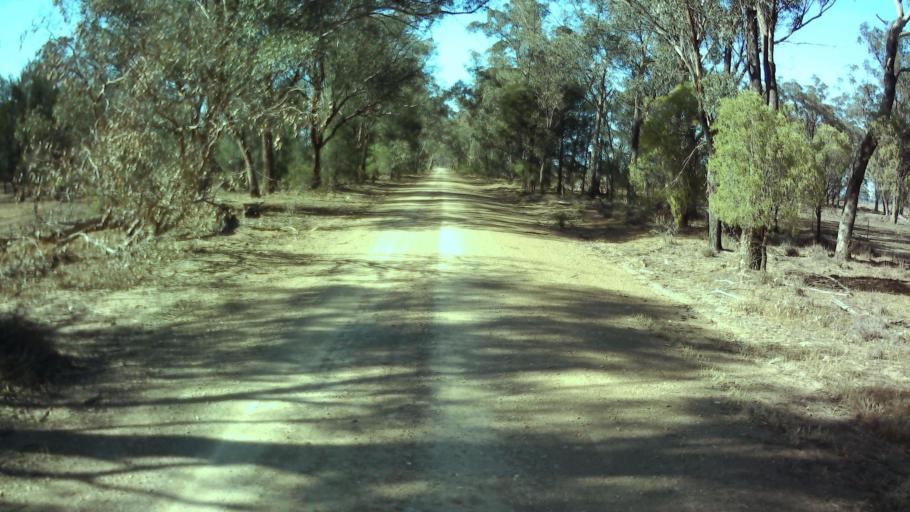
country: AU
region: New South Wales
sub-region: Weddin
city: Grenfell
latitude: -33.9391
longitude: 147.8713
